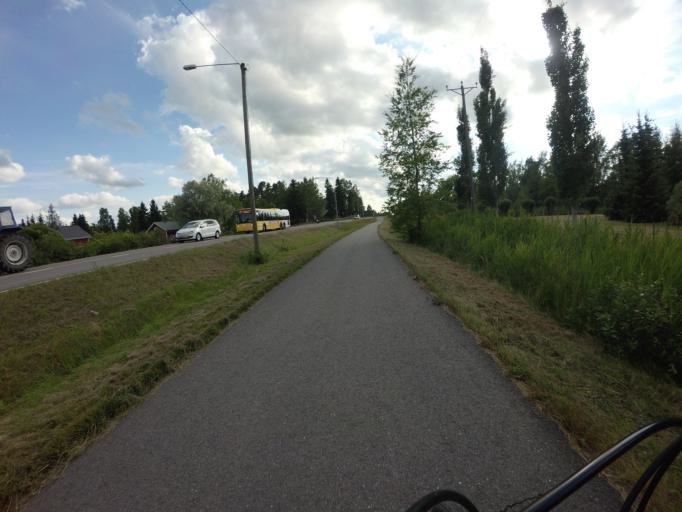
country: FI
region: Varsinais-Suomi
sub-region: Turku
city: Vahto
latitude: 60.5928
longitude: 22.3834
